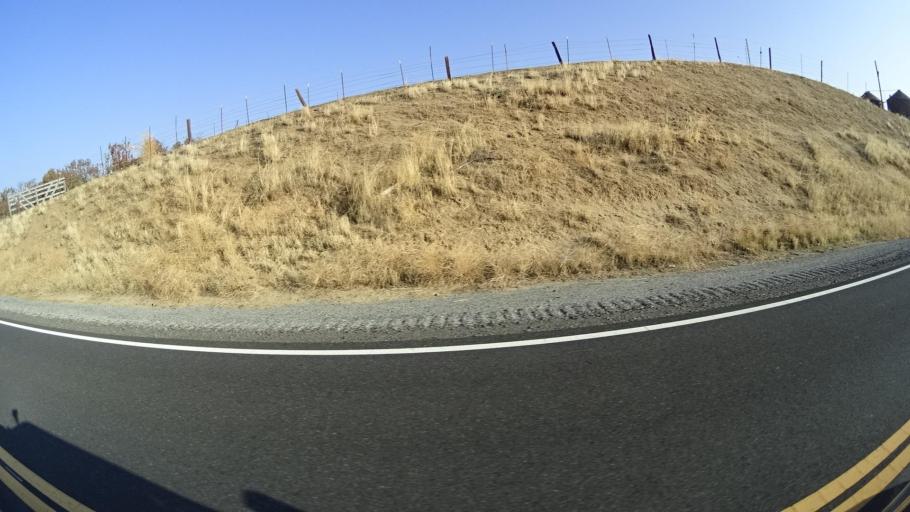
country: US
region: California
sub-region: Tulare County
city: Richgrove
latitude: 35.7610
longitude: -119.0315
